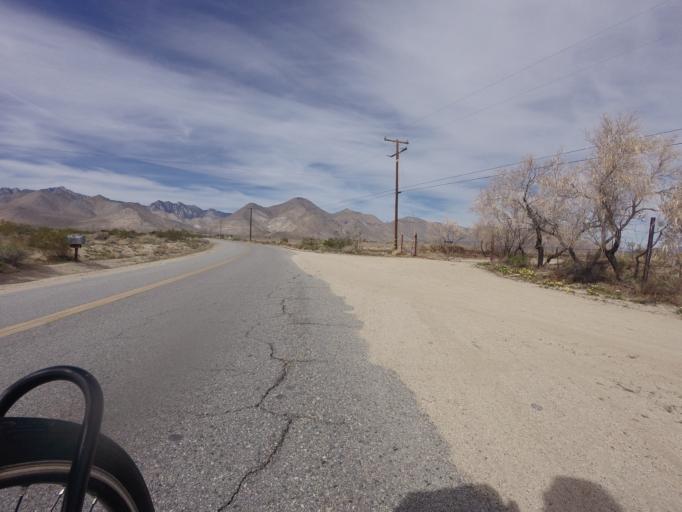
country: US
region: California
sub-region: Kern County
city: Inyokern
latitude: 35.7762
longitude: -117.8525
